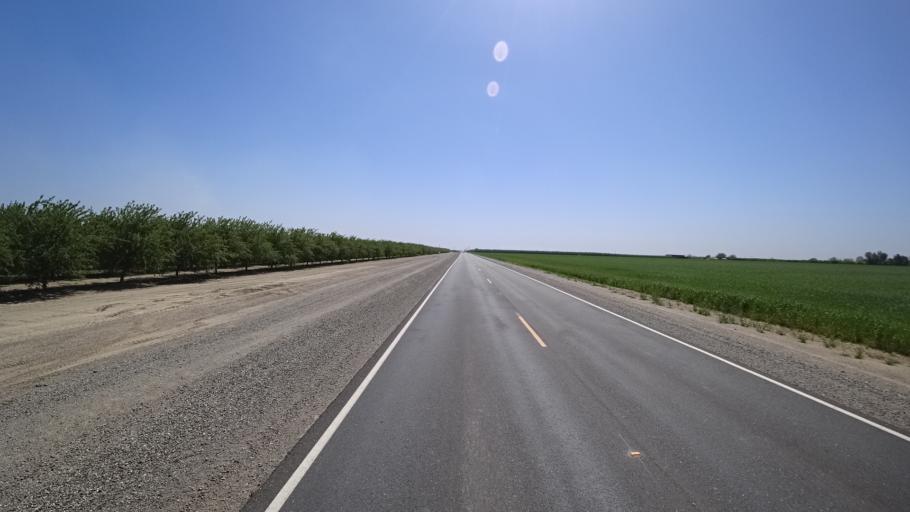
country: US
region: California
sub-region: Glenn County
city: Willows
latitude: 39.5880
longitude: -122.1371
